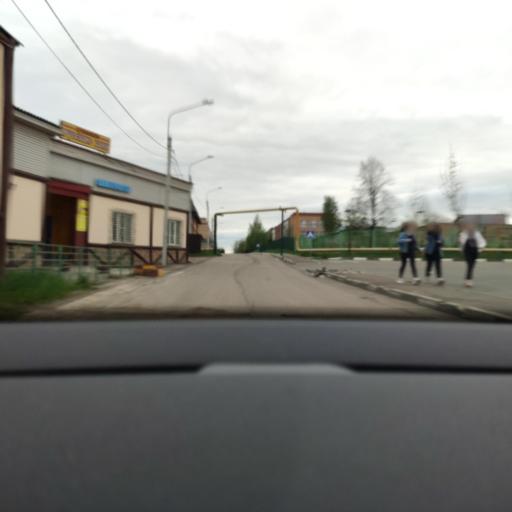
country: RU
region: Moskovskaya
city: Novopodrezkovo
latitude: 55.9939
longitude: 37.3439
